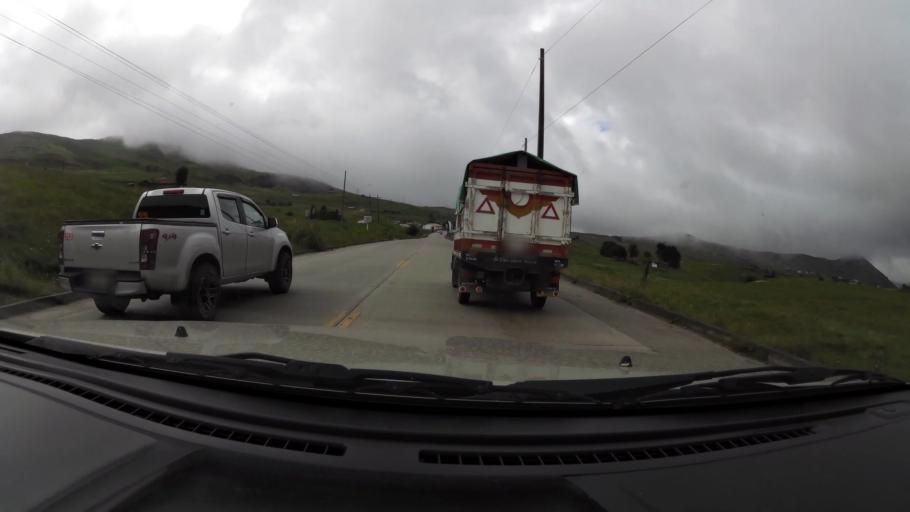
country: EC
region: Canar
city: Canar
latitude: -2.6076
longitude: -78.9179
